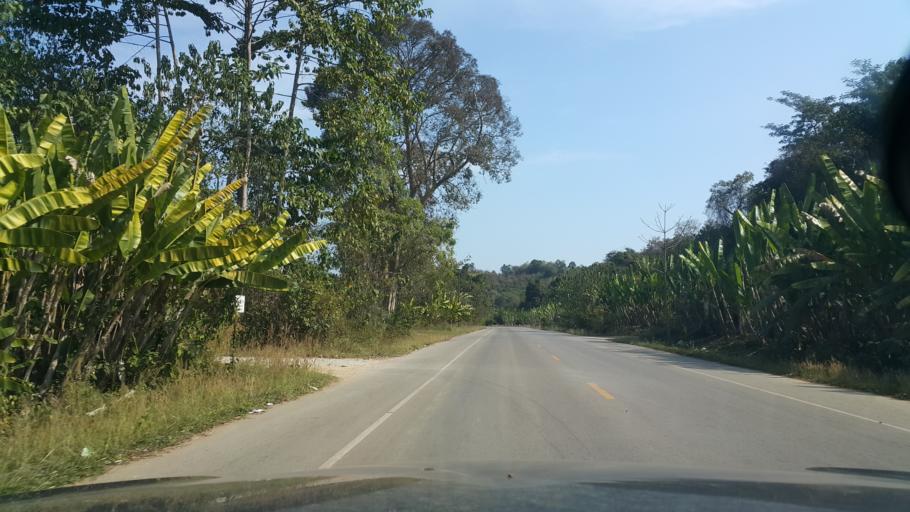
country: TH
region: Loei
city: Pak Chom
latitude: 18.0919
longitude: 101.9585
